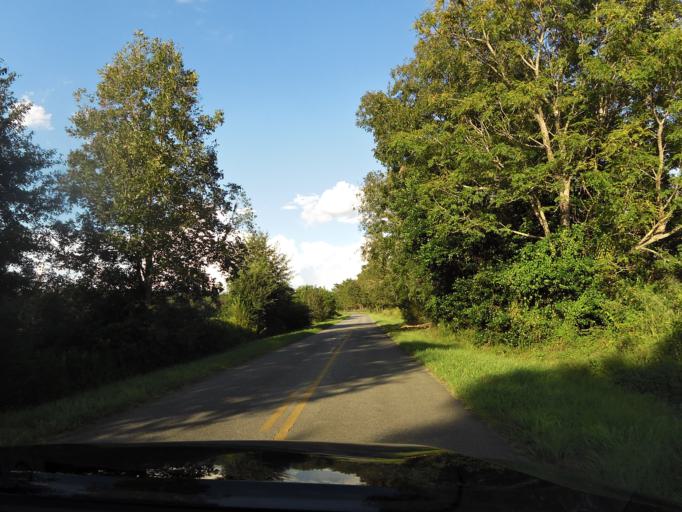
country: US
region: Georgia
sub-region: Lowndes County
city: Remerton
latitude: 30.7949
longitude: -83.3901
